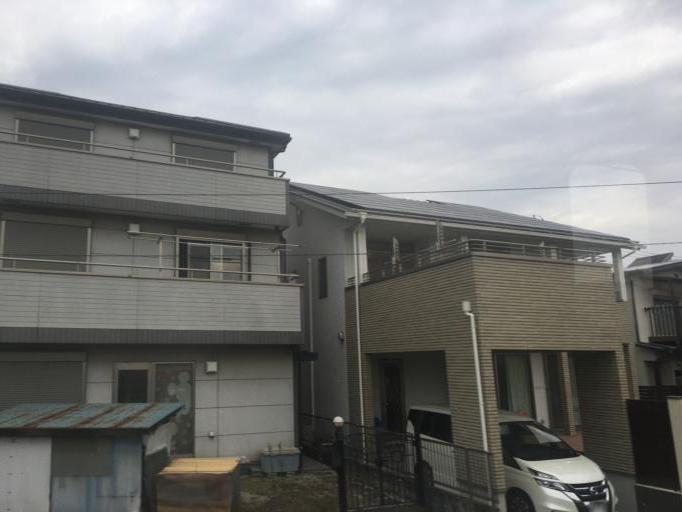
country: JP
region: Saitama
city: Hanno
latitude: 35.8460
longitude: 139.3298
